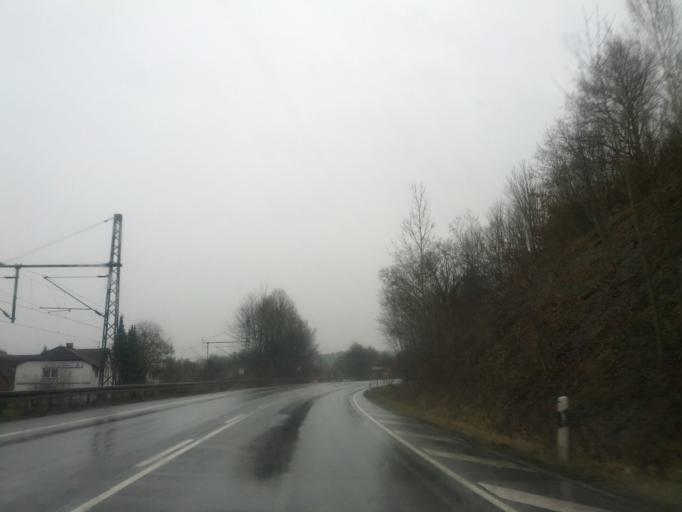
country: DE
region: Hesse
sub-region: Regierungsbezirk Kassel
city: Bad Sooden-Allendorf
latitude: 51.2273
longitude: 9.9906
